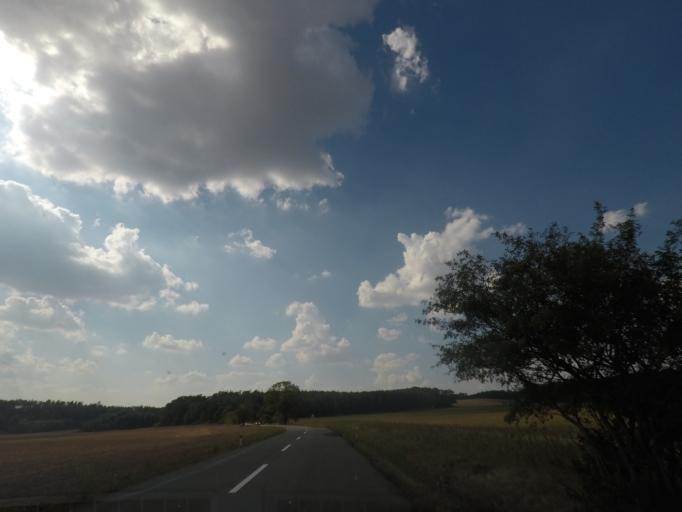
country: CZ
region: Kralovehradecky
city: Trebechovice pod Orebem
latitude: 50.2186
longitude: 15.9813
